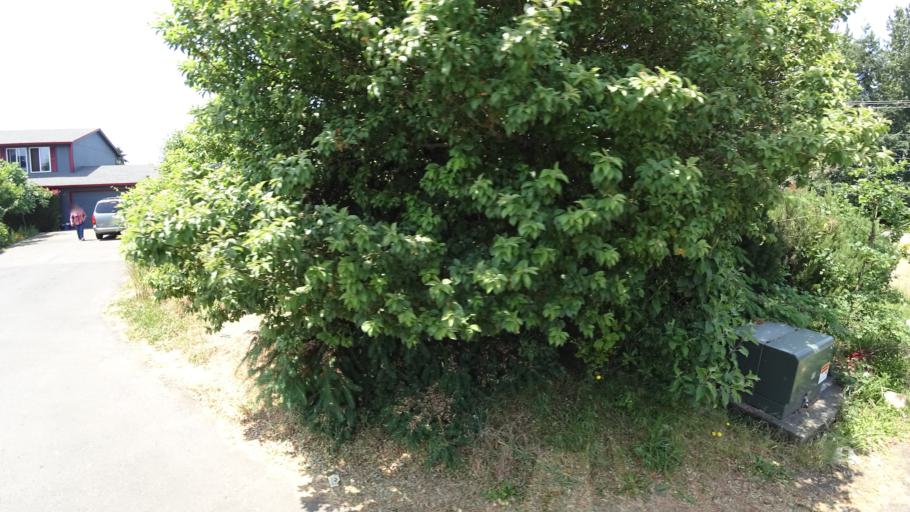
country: US
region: Oregon
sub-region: Washington County
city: Hillsboro
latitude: 45.4992
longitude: -122.9386
